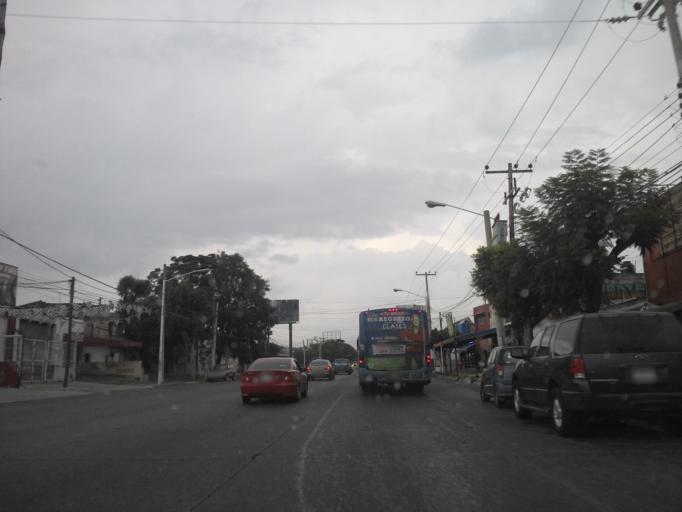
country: MX
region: Jalisco
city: Guadalajara
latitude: 20.6328
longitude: -103.3675
